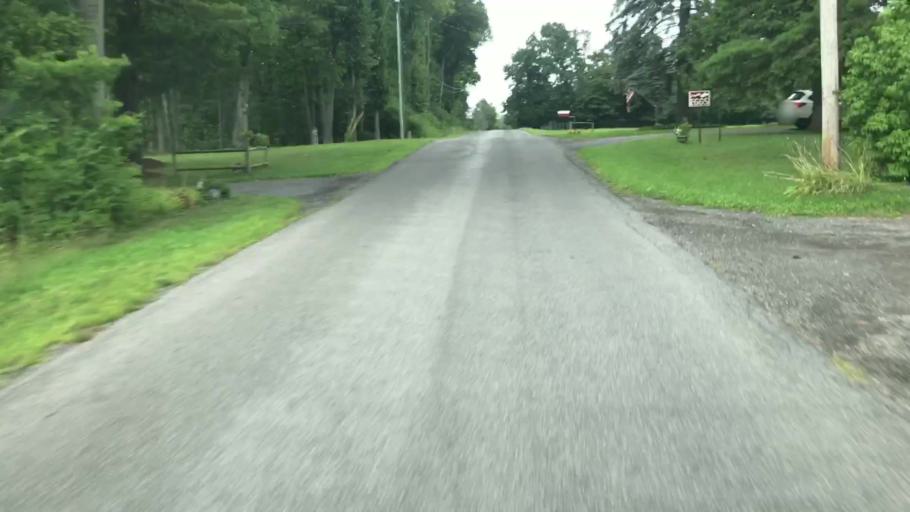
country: US
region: New York
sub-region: Cayuga County
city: Melrose Park
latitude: 42.9590
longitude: -76.5068
